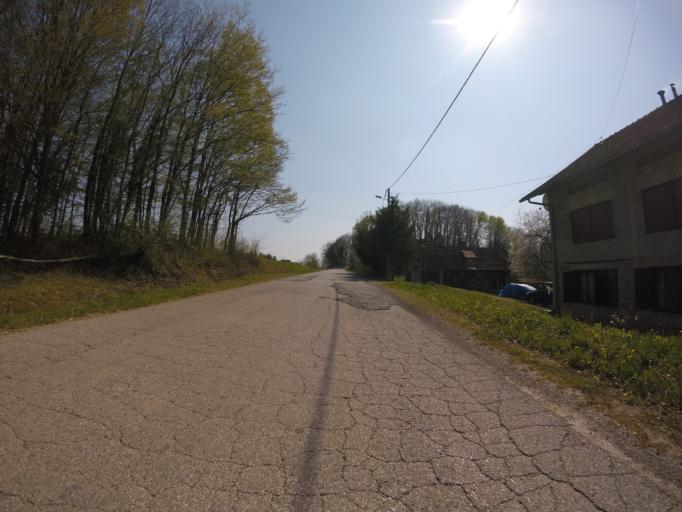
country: HR
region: Grad Zagreb
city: Strmec
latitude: 45.6181
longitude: 15.9496
